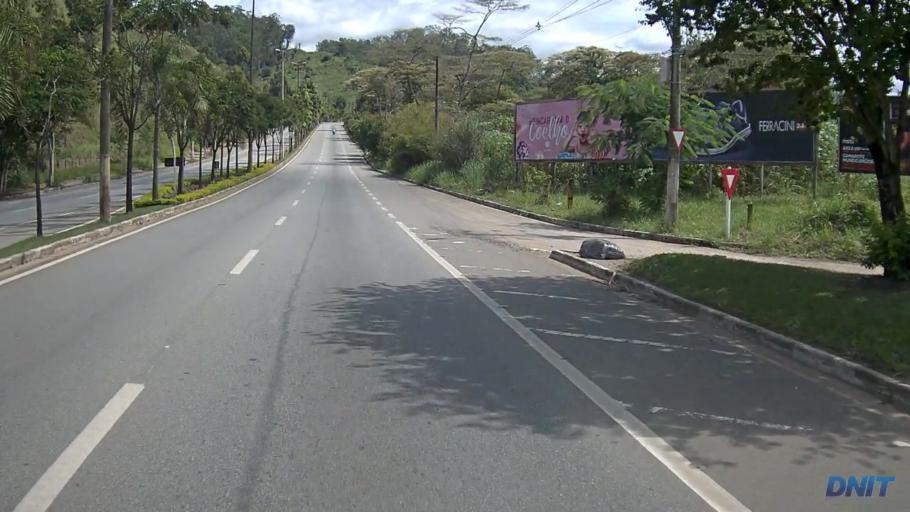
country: BR
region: Minas Gerais
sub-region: Coronel Fabriciano
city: Coronel Fabriciano
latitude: -19.5082
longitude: -42.5803
